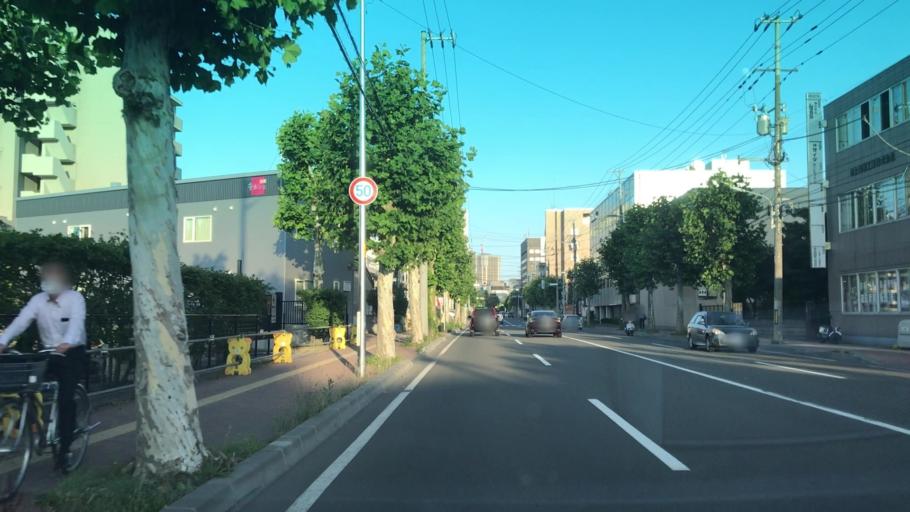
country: JP
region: Hokkaido
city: Sapporo
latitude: 43.0737
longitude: 141.3270
